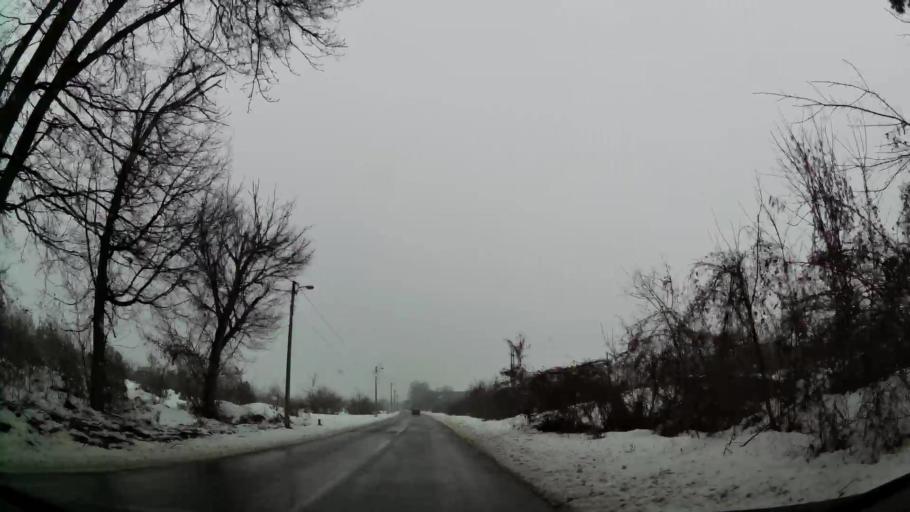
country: RS
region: Central Serbia
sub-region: Belgrade
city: Surcin
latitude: 44.8630
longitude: 20.3220
